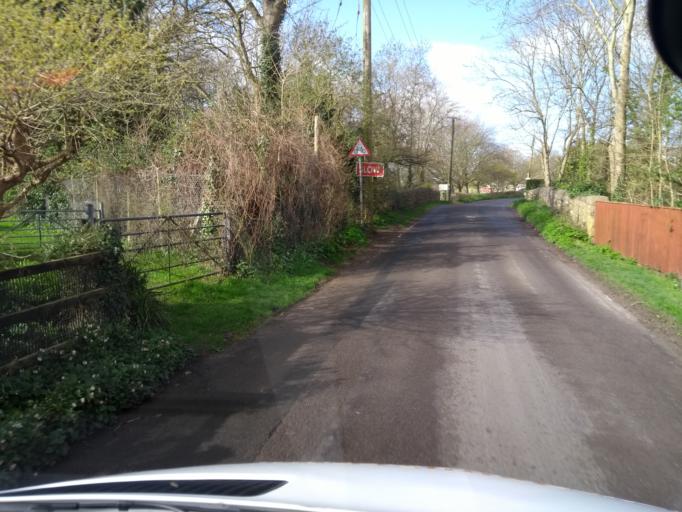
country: GB
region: England
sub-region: Somerset
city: Woolavington
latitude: 51.1604
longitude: -2.9243
